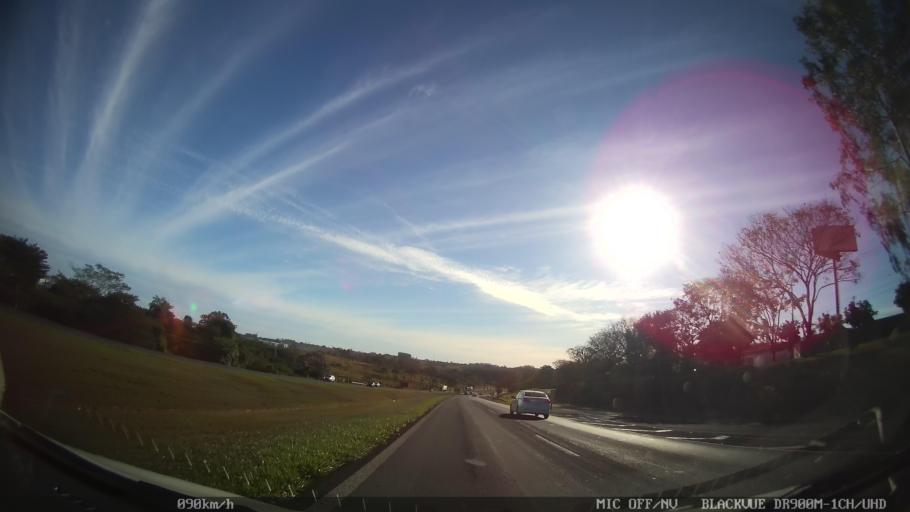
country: BR
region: Sao Paulo
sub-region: Sao Jose Do Rio Preto
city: Sao Jose do Rio Preto
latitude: -20.8215
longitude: -49.4263
